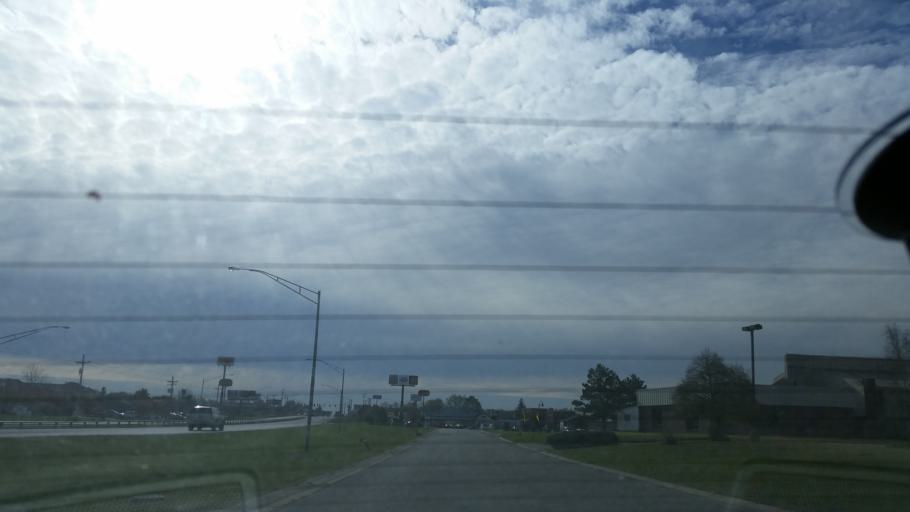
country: US
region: Indiana
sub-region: Howard County
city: Indian Heights
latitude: 40.4379
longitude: -86.1274
